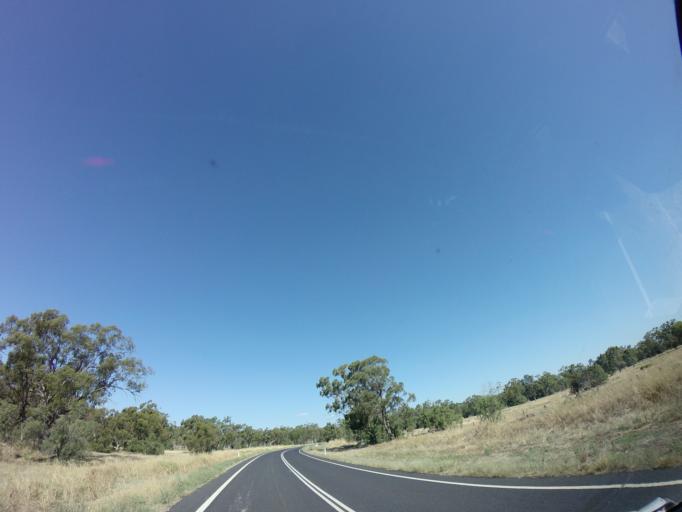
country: AU
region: New South Wales
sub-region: Narromine
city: Narromine
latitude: -31.6417
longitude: 147.9094
